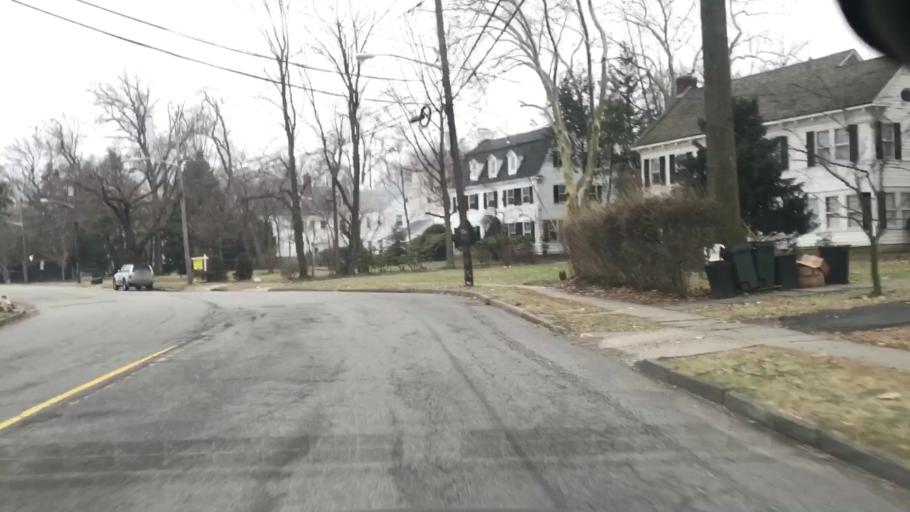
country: US
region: New Jersey
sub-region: Union County
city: Hillside
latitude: 40.6836
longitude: -74.2188
